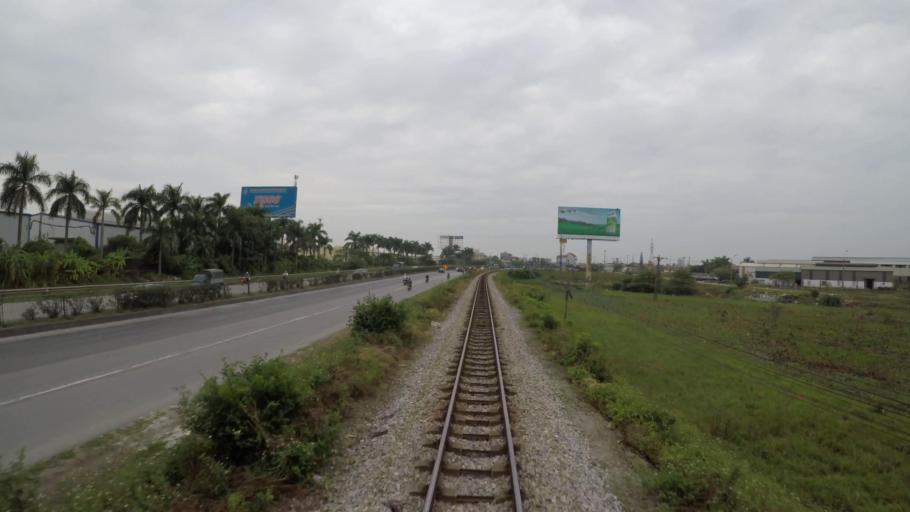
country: VN
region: Hai Duong
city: Thanh Pho Hai Duong
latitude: 20.9624
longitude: 106.3727
